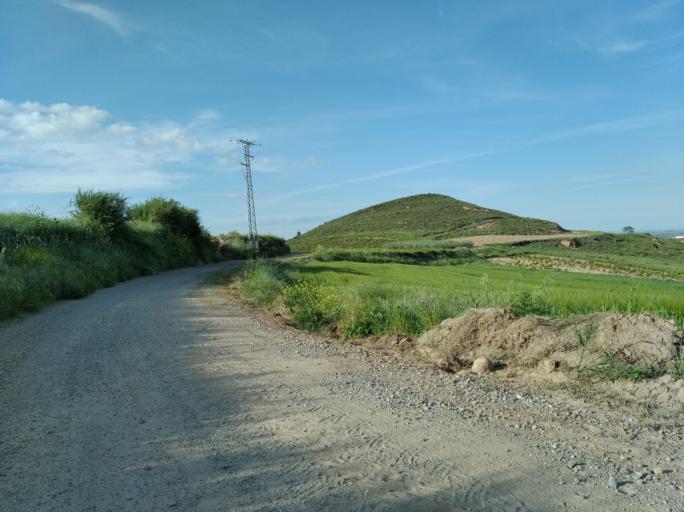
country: ES
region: La Rioja
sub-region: Provincia de La Rioja
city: Sojuela
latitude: 42.3721
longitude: -2.5448
